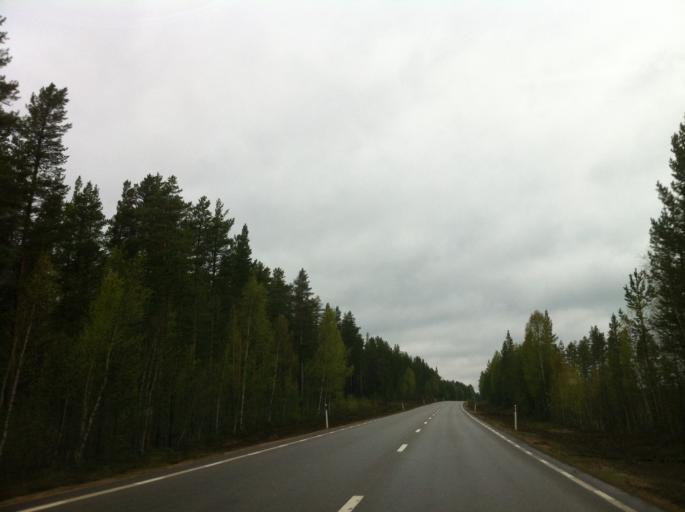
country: SE
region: Jaemtland
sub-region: Harjedalens Kommun
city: Sveg
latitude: 62.1114
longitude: 14.1851
